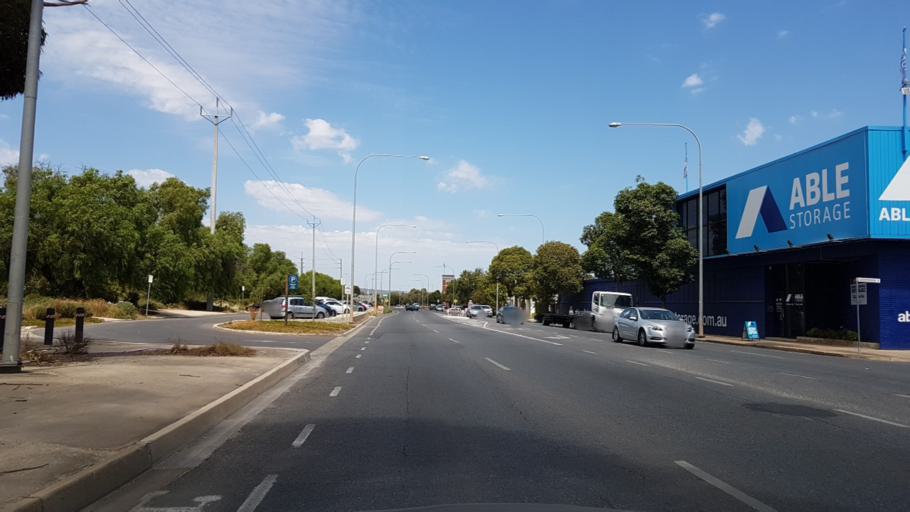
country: AU
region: South Australia
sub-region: City of West Torrens
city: Thebarton
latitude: -34.9204
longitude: 138.5790
